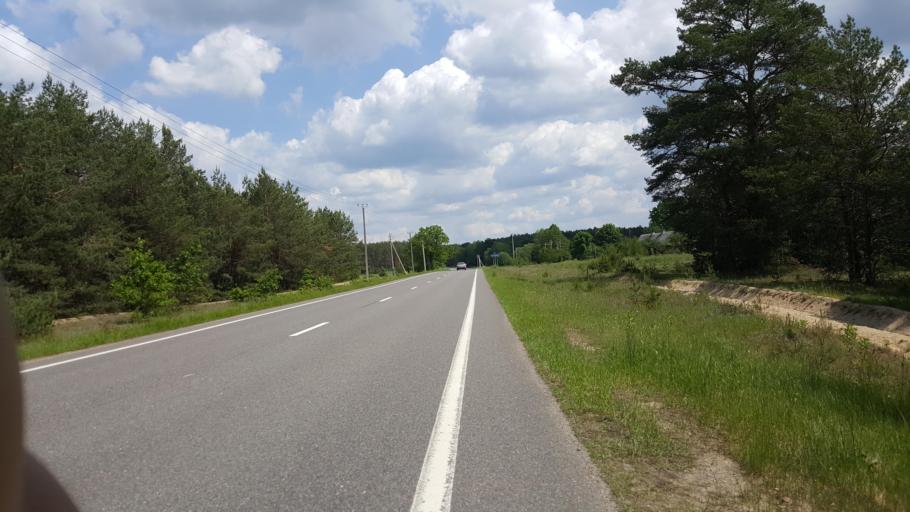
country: BY
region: Brest
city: Zhabinka
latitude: 52.4129
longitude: 24.1132
